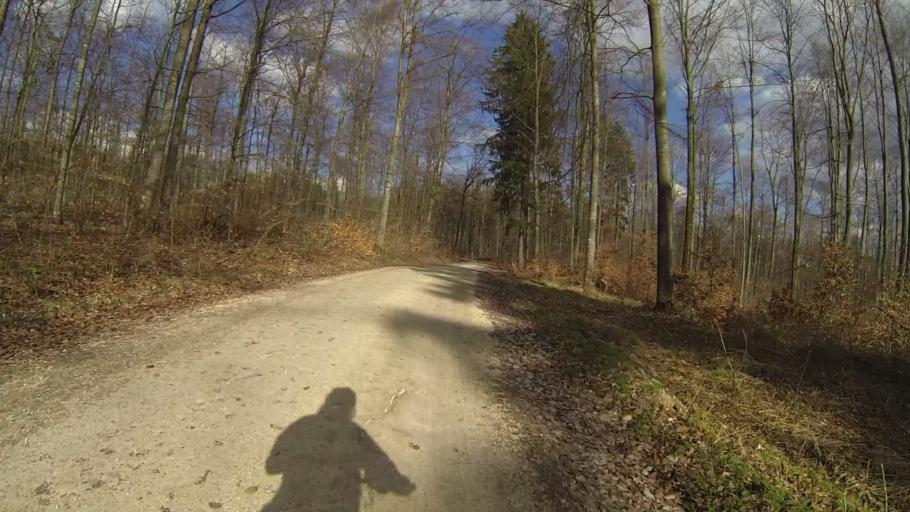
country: DE
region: Baden-Wuerttemberg
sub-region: Regierungsbezirk Stuttgart
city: Heidenheim an der Brenz
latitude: 48.6994
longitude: 10.1194
